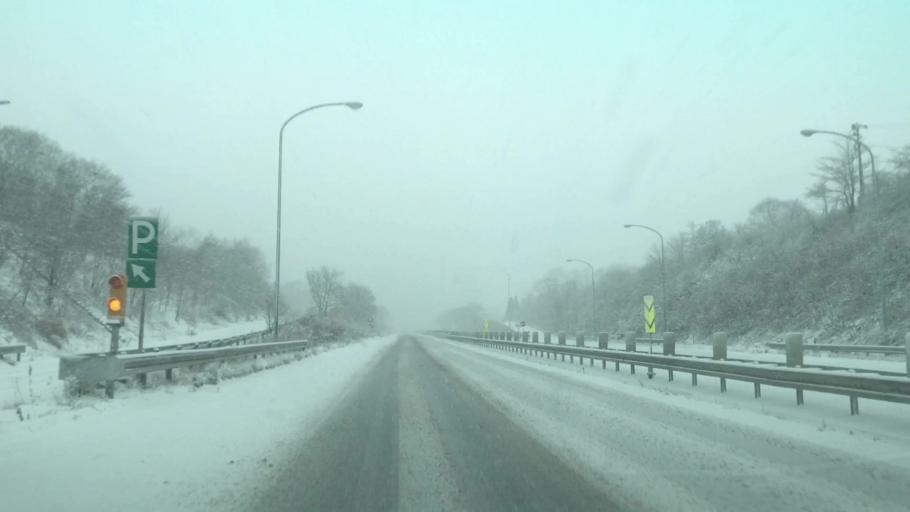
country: JP
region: Hokkaido
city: Muroran
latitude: 42.4450
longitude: 141.1510
